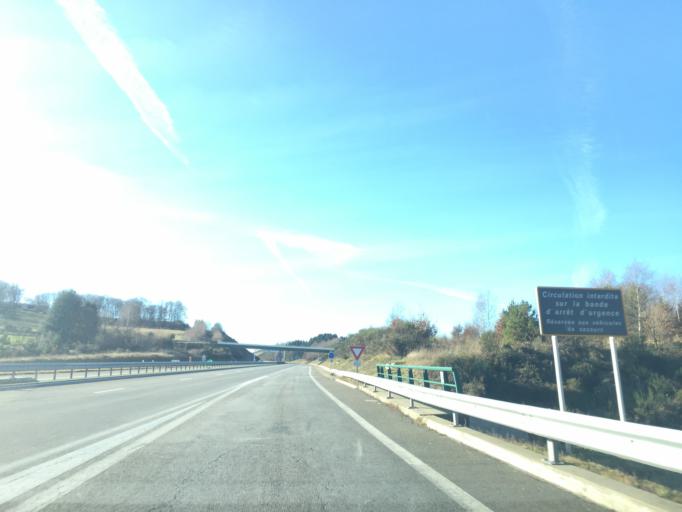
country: FR
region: Auvergne
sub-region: Departement du Puy-de-Dome
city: Chapdes-Beaufort
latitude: 45.8341
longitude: 2.8176
